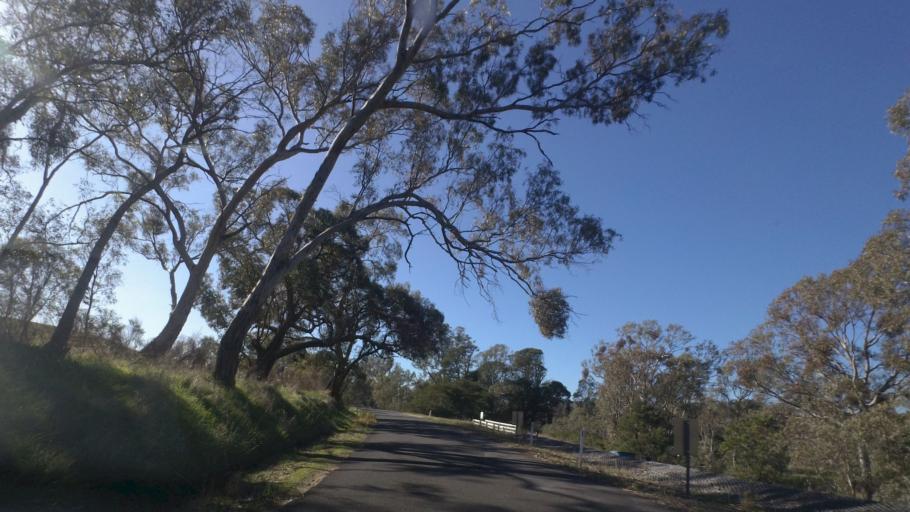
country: AU
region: Victoria
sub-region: Mount Alexander
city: Castlemaine
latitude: -36.9672
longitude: 144.3239
